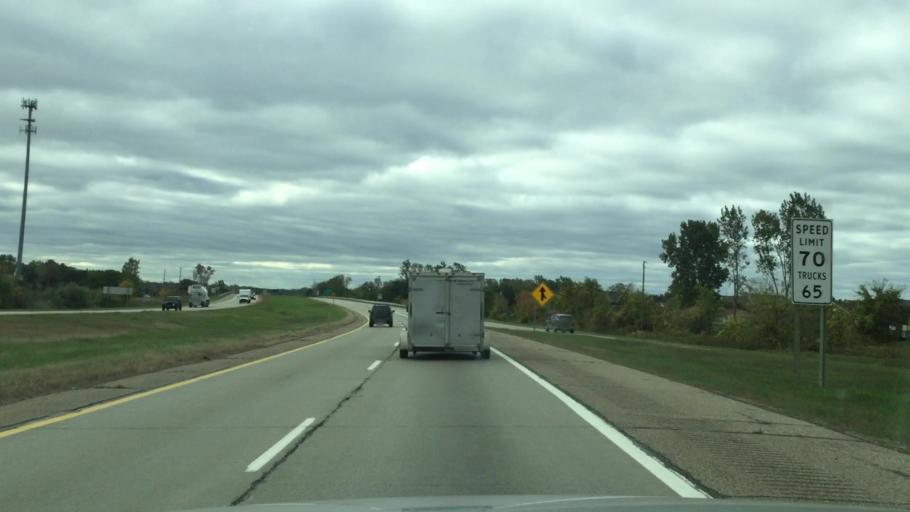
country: US
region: Michigan
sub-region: Macomb County
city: Shelby
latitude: 42.7326
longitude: -83.0267
